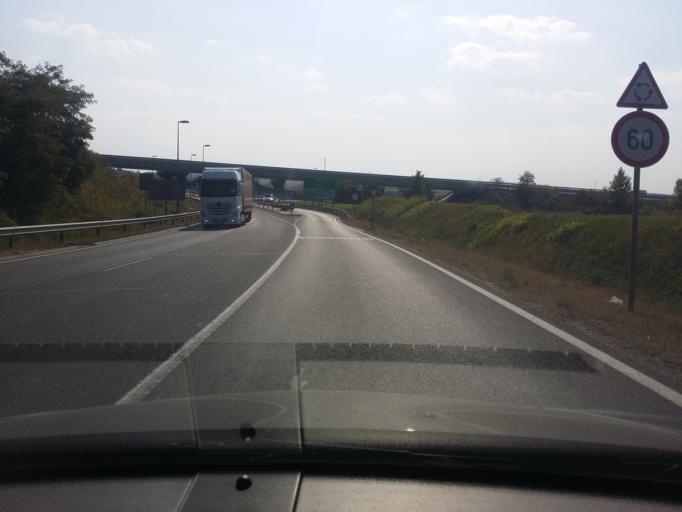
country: HU
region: Fejer
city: Baracs
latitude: 46.9121
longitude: 18.9264
